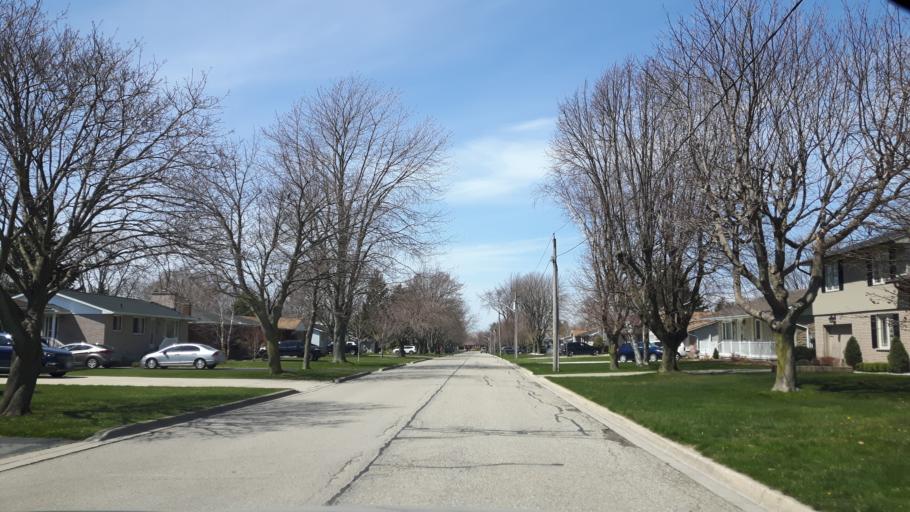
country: CA
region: Ontario
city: Goderich
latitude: 43.7327
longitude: -81.7166
